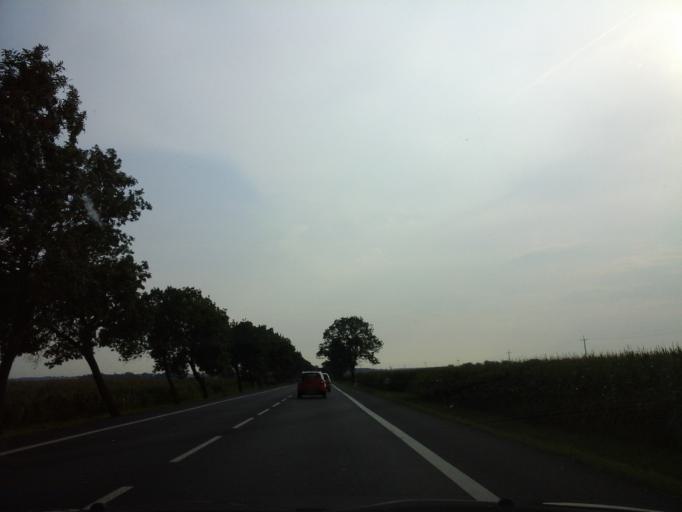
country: PL
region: Greater Poland Voivodeship
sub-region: Powiat koscianski
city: Bojanowo Stare
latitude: 52.0507
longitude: 16.5738
